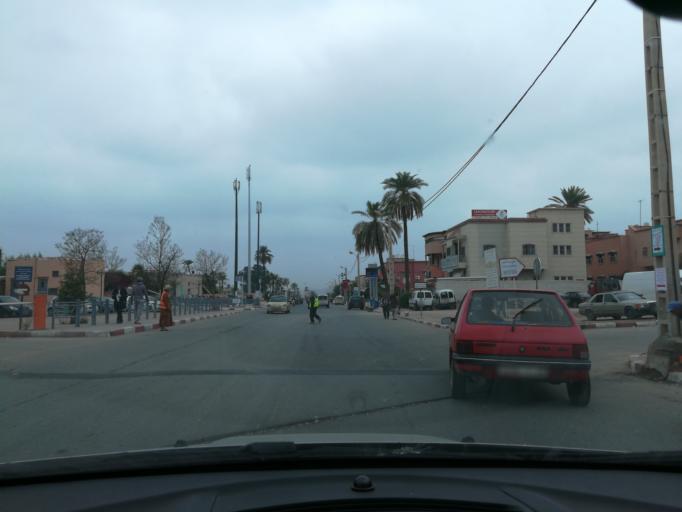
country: MA
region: Marrakech-Tensift-Al Haouz
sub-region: Marrakech
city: Marrakesh
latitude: 31.6647
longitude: -7.9945
